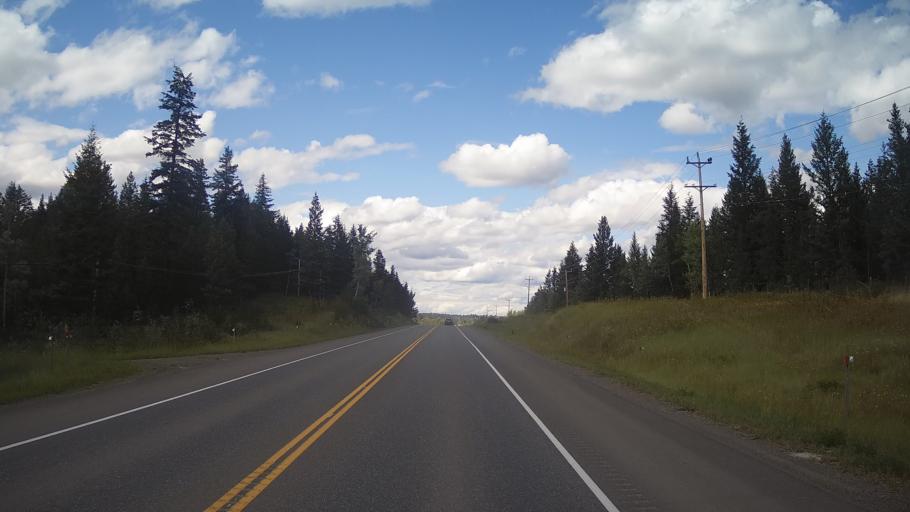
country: CA
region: British Columbia
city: Cache Creek
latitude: 51.6935
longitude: -121.3188
